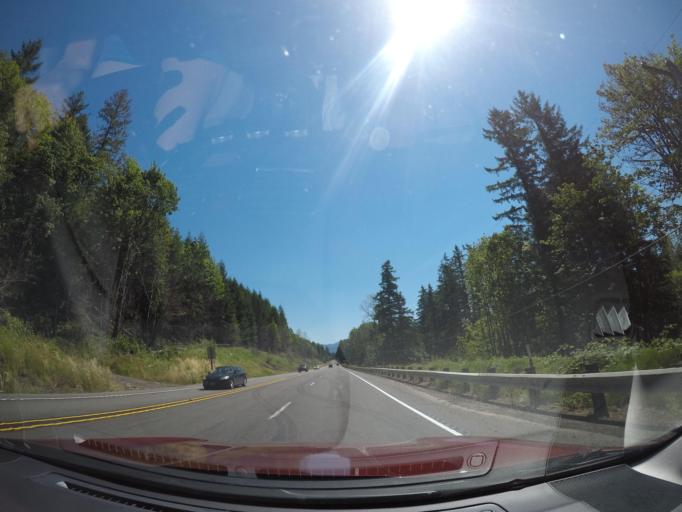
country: US
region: Oregon
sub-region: Linn County
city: Mill City
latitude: 44.7563
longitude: -122.4579
